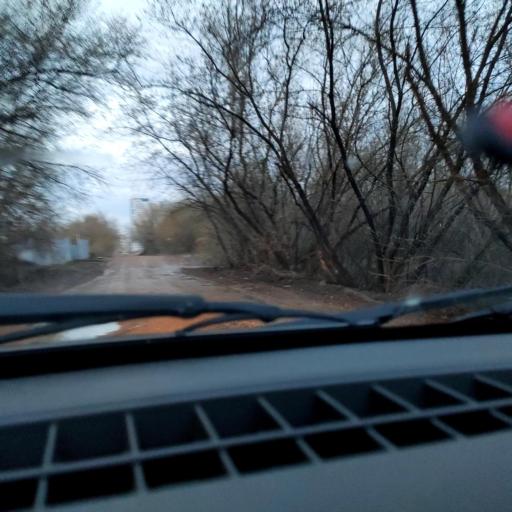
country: RU
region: Bashkortostan
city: Ufa
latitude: 54.6780
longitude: 55.9766
